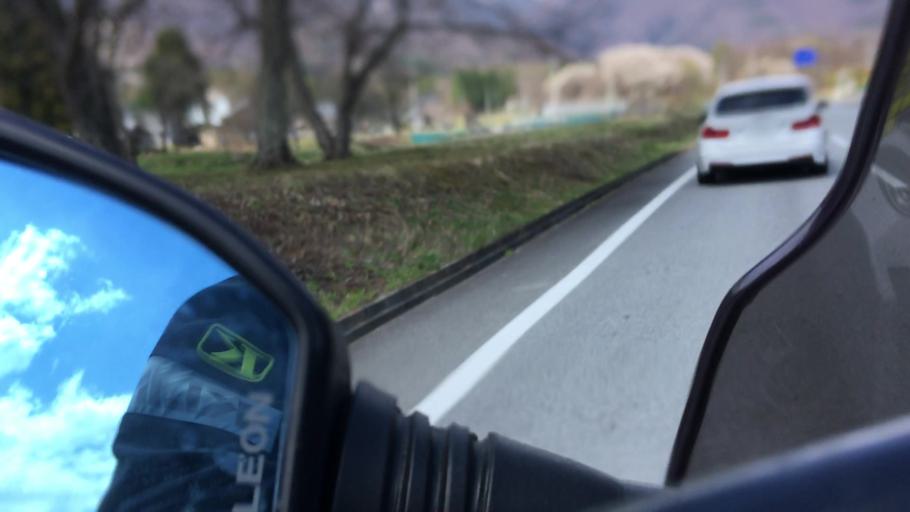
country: JP
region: Yamanashi
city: Nirasaki
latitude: 35.7827
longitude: 138.3224
